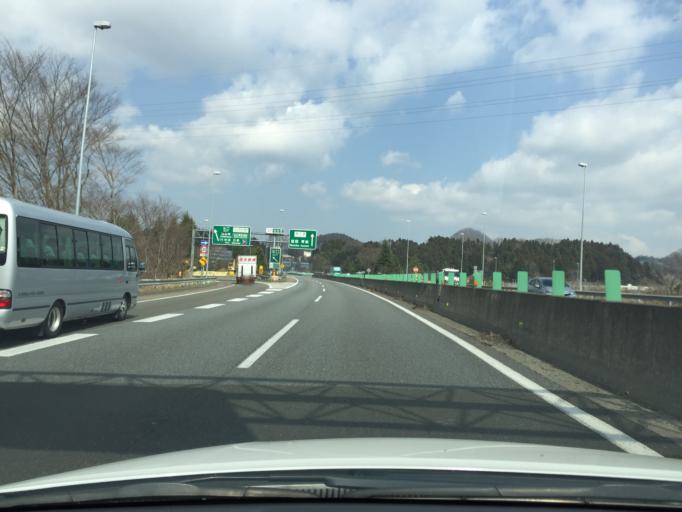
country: JP
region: Miyagi
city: Sendai
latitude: 38.2125
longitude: 140.8046
